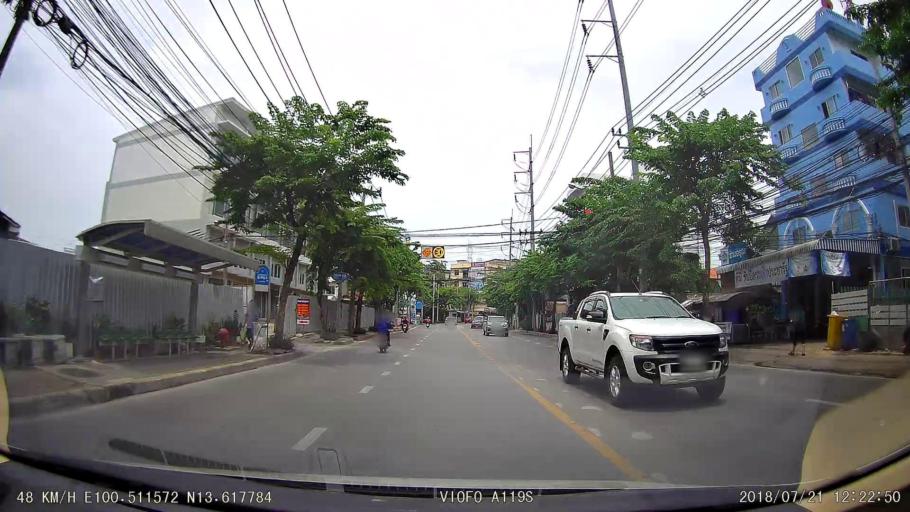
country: TH
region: Bangkok
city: Thung Khru
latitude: 13.6176
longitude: 100.5116
